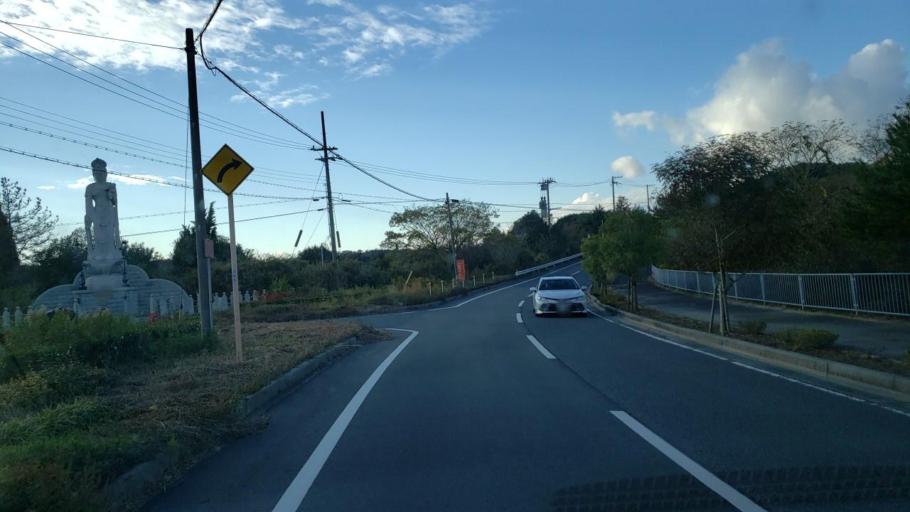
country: JP
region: Hyogo
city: Akashi
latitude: 34.5759
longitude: 134.9919
